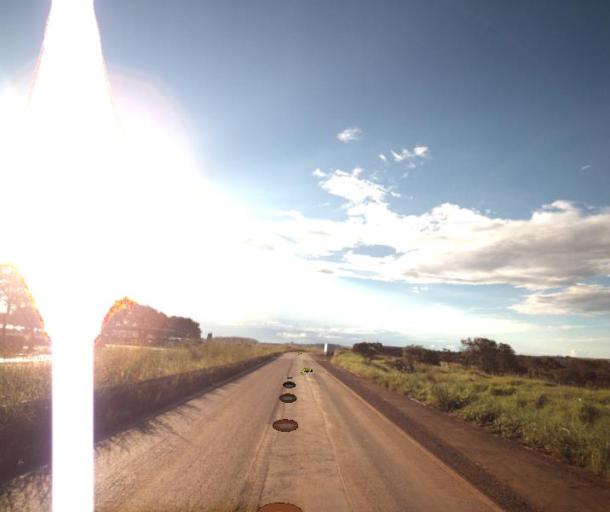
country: BR
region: Goias
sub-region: Anapolis
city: Anapolis
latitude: -16.2556
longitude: -48.9909
